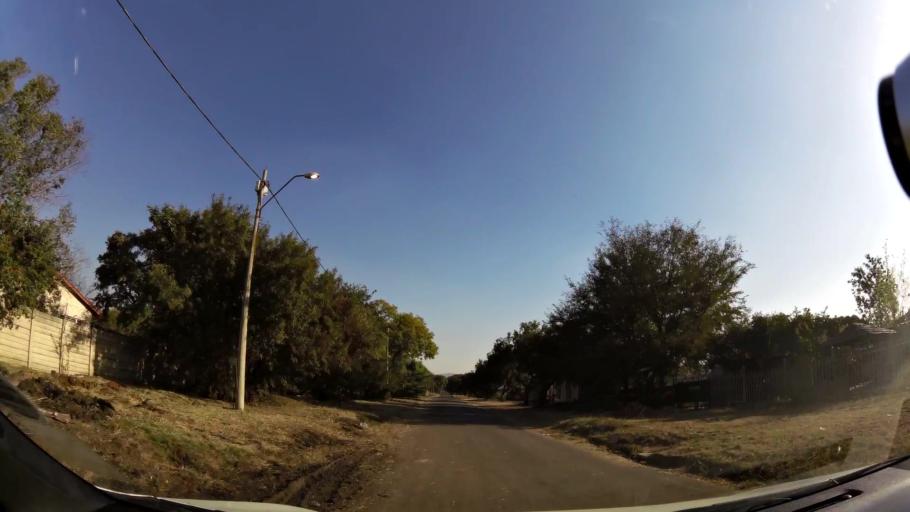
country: ZA
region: North-West
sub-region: Bojanala Platinum District Municipality
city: Rustenburg
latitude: -25.6589
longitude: 27.2623
